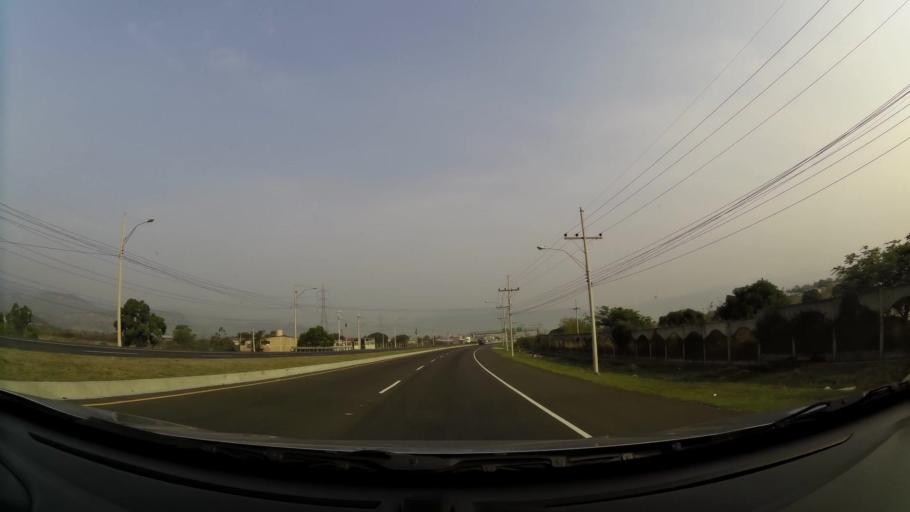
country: HN
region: Francisco Morazan
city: Tamara
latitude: 14.1996
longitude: -87.3441
